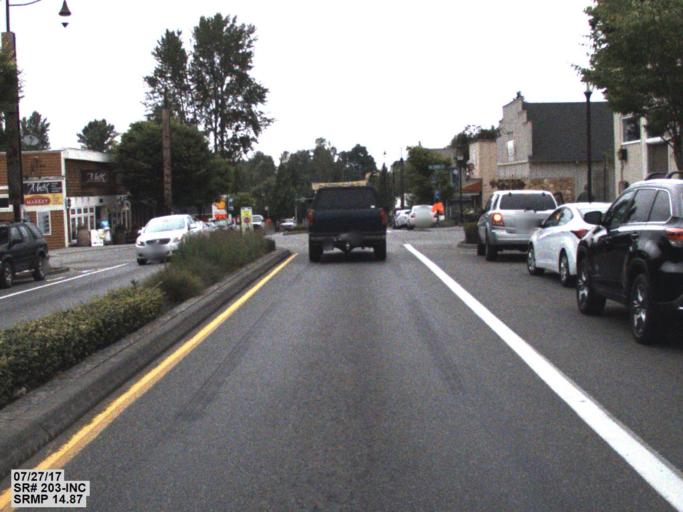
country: US
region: Washington
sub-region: King County
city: Duvall
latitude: 47.7414
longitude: -121.9859
